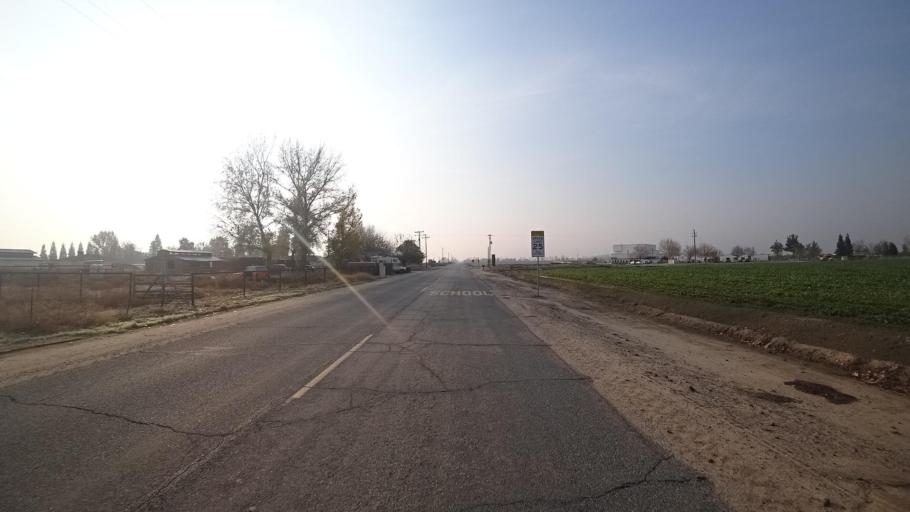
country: US
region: California
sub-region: Kern County
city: Greenfield
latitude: 35.2242
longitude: -119.0215
